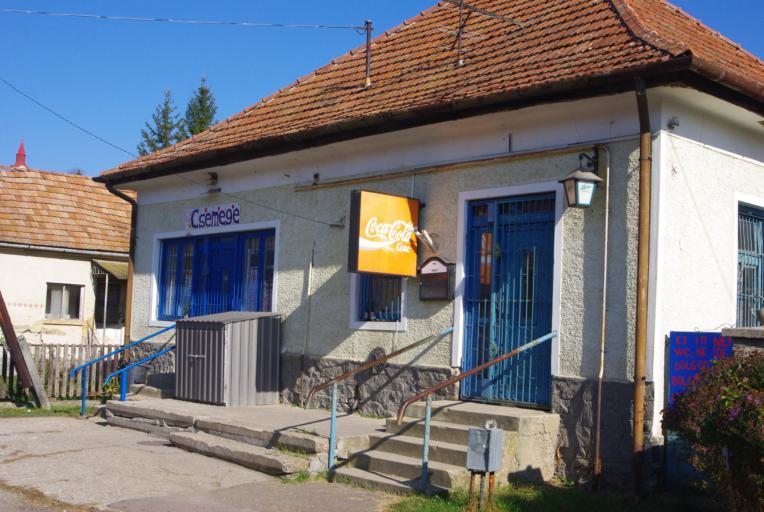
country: HU
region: Borsod-Abauj-Zemplen
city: Borsodnadasd
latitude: 48.0522
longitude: 20.2690
